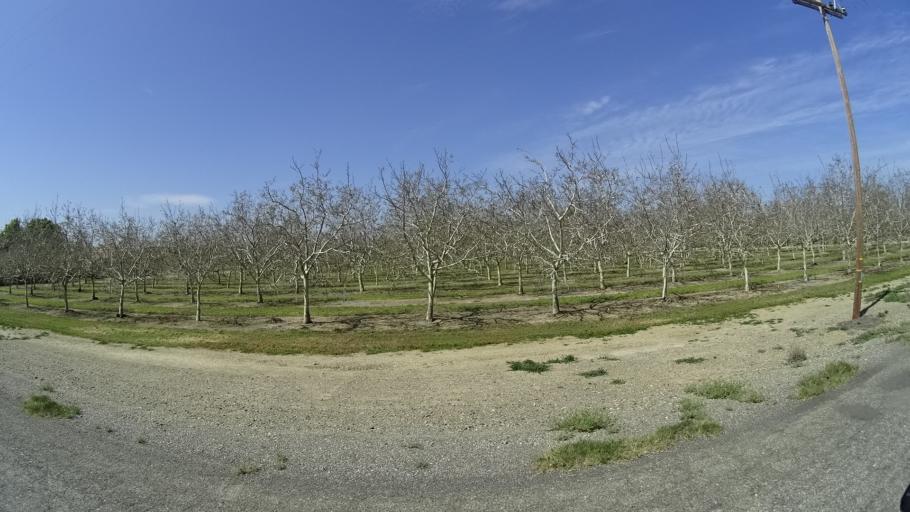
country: US
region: California
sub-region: Glenn County
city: Hamilton City
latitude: 39.6449
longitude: -122.0743
